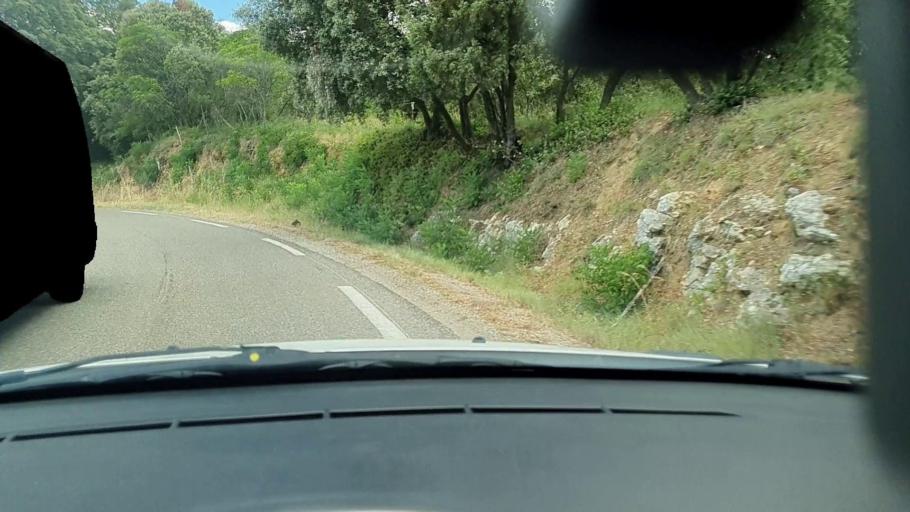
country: FR
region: Languedoc-Roussillon
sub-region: Departement du Gard
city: Cabrieres
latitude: 43.9238
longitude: 4.4737
